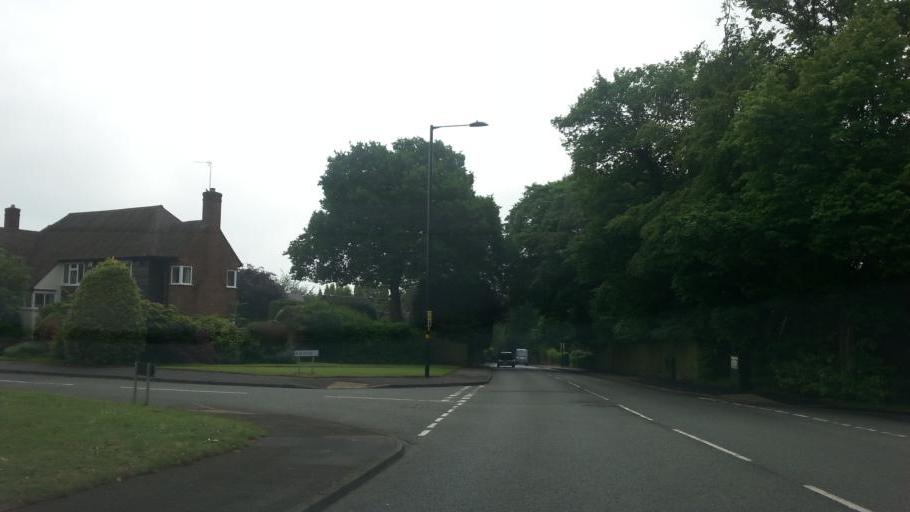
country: GB
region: England
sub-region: City and Borough of Birmingham
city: Sutton Coldfield
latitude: 52.5843
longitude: -1.8374
